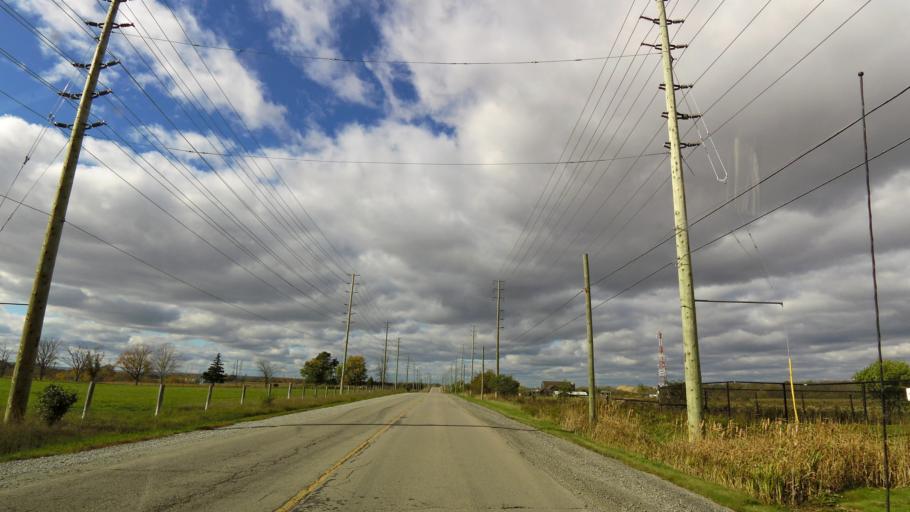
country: CA
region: Ontario
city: Oakville
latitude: 43.4963
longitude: -79.7521
